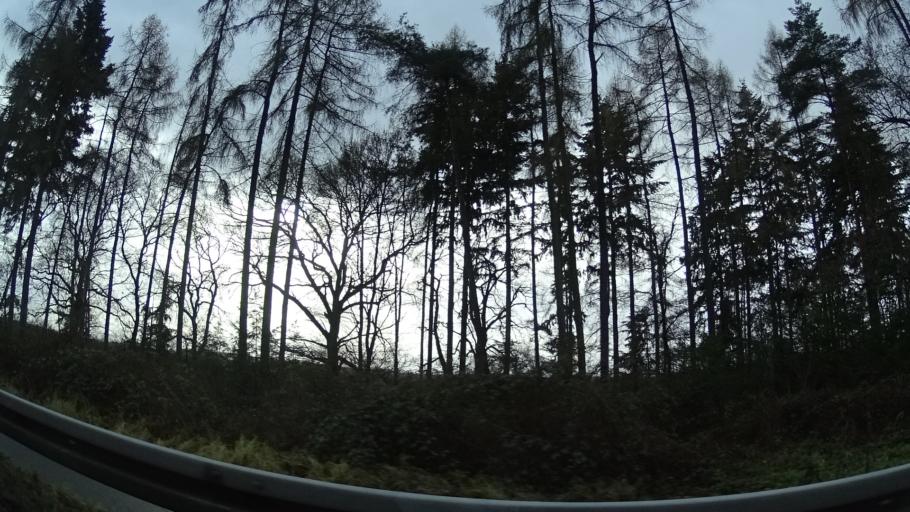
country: DE
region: Hesse
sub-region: Regierungsbezirk Giessen
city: Lich
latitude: 50.5268
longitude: 8.7869
